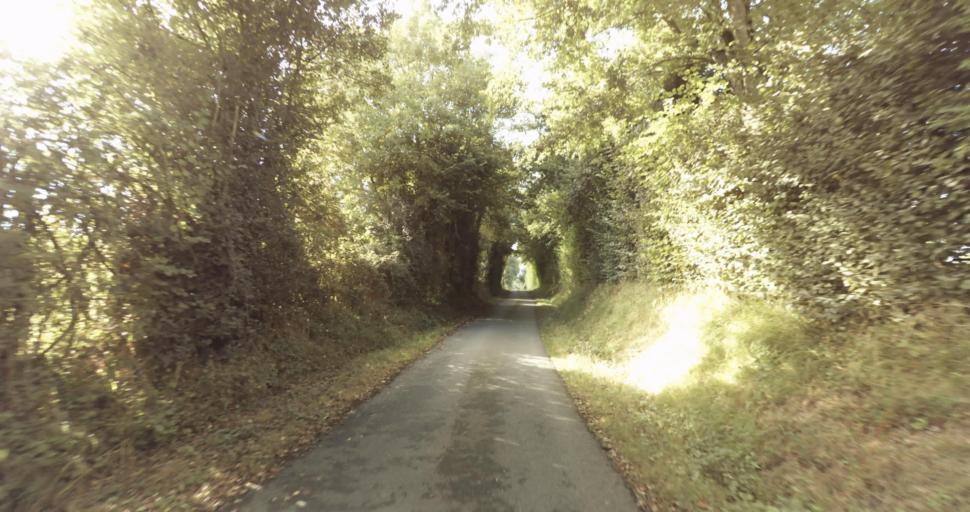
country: FR
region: Lower Normandy
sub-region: Departement de l'Orne
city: Vimoutiers
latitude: 48.9148
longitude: 0.1247
